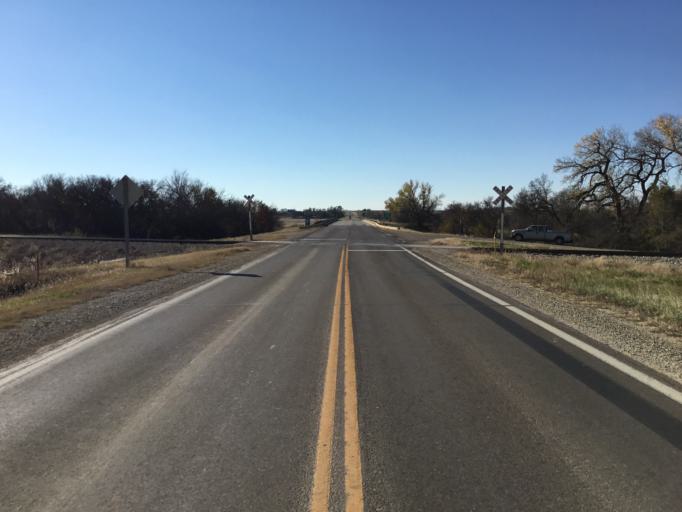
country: US
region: Kansas
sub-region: Lincoln County
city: Lincoln
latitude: 39.0294
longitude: -98.1502
